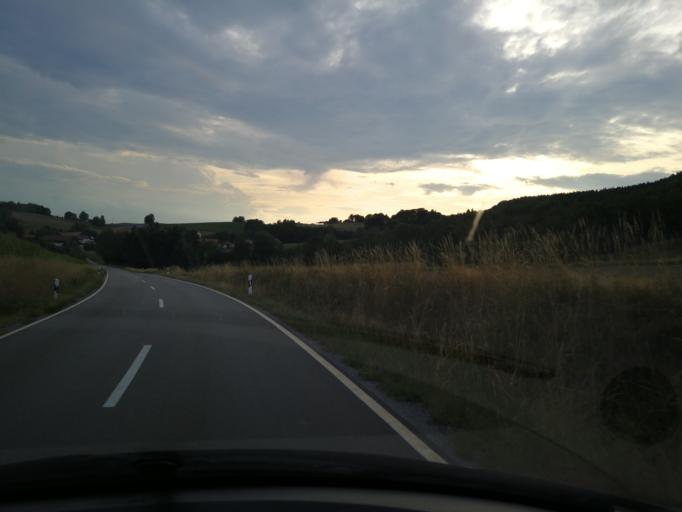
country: DE
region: Bavaria
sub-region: Lower Bavaria
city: Rattiszell
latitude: 49.0381
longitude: 12.6890
